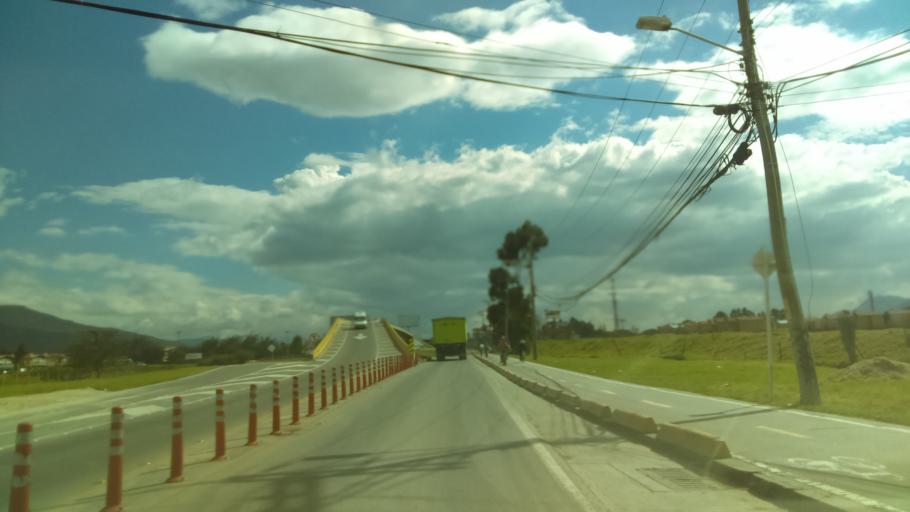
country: CO
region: Cundinamarca
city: Cajica
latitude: 4.9019
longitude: -74.0306
